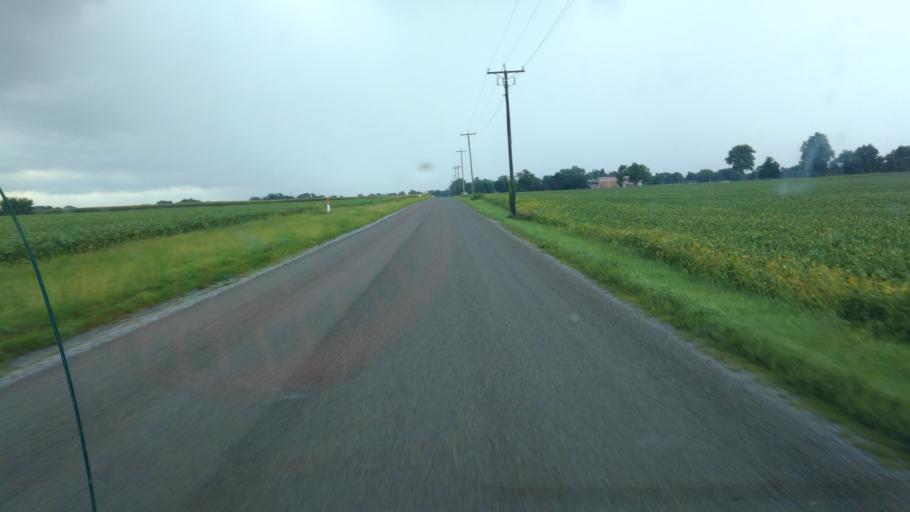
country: US
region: Ohio
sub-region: Hardin County
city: Kenton
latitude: 40.6548
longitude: -83.5761
